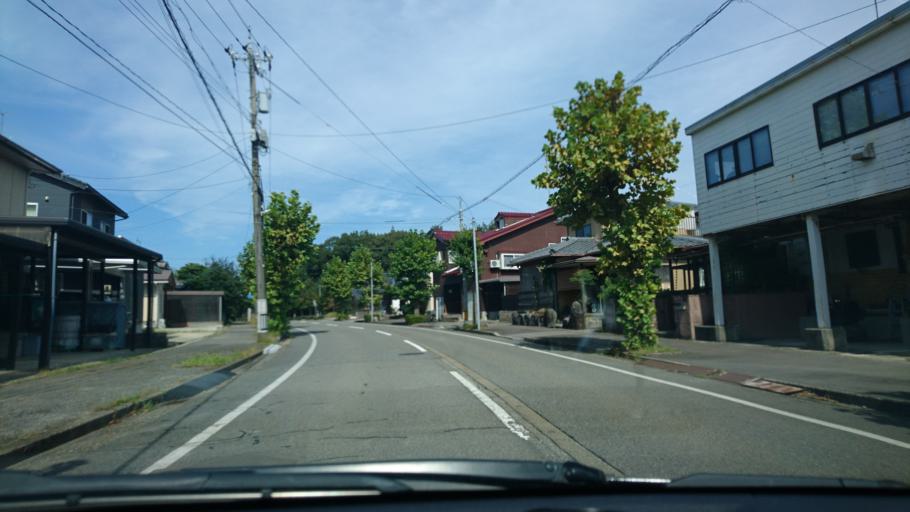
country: JP
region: Ishikawa
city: Komatsu
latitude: 36.3258
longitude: 136.3476
